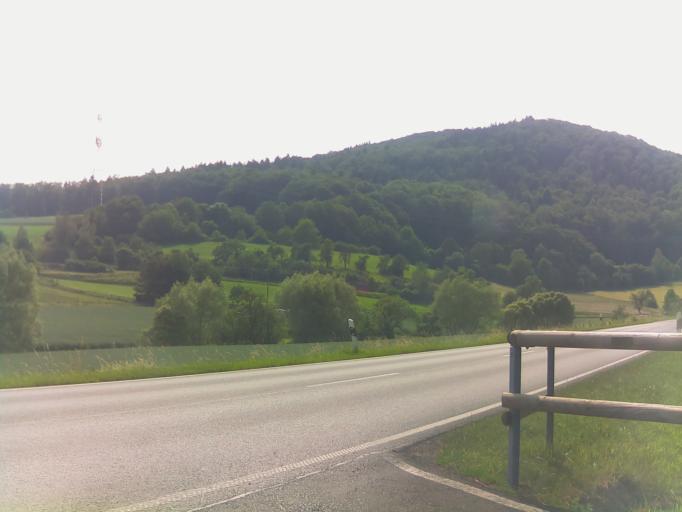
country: DE
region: Hesse
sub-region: Regierungsbezirk Kassel
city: Waldeck
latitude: 51.1812
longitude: 9.0906
